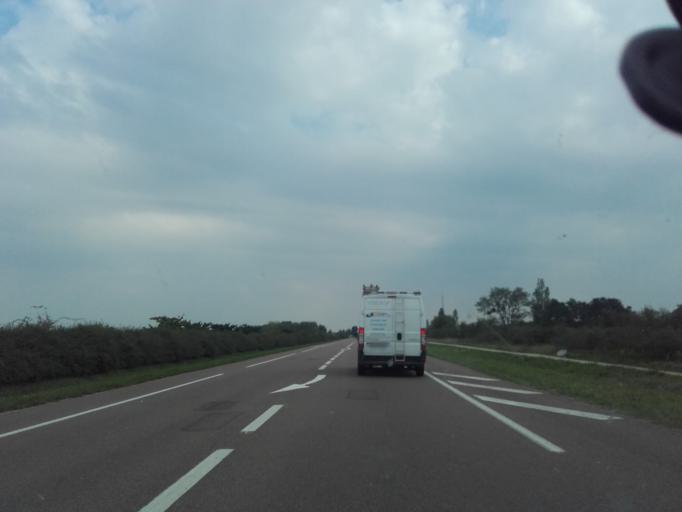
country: FR
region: Bourgogne
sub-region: Departement de la Cote-d'Or
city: Bligny-les-Beaune
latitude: 47.0106
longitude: 4.8178
